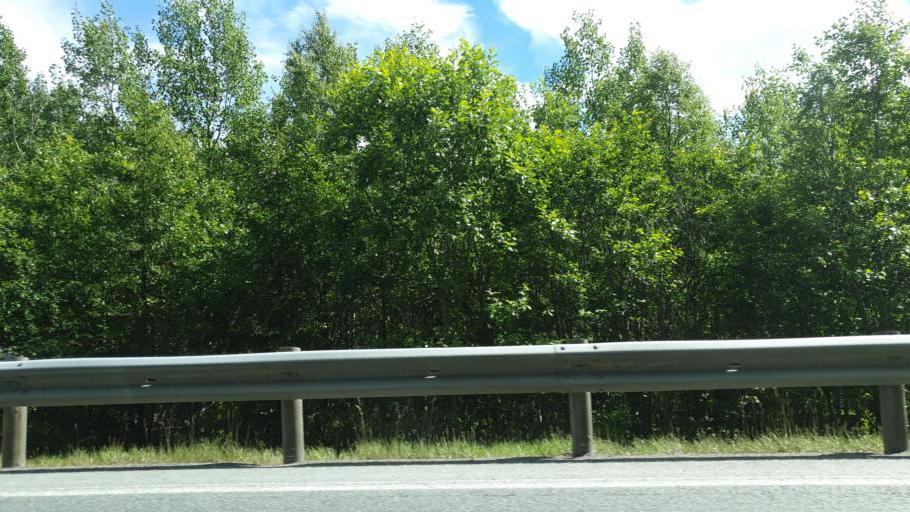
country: NO
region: Sor-Trondelag
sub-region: Rennebu
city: Berkak
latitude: 62.7172
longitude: 9.9646
